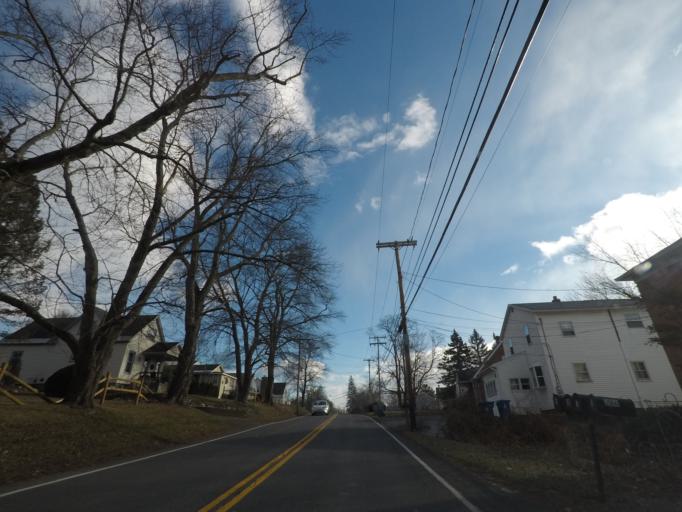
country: US
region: New York
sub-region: Schenectady County
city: Niskayuna
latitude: 42.7607
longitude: -73.8867
